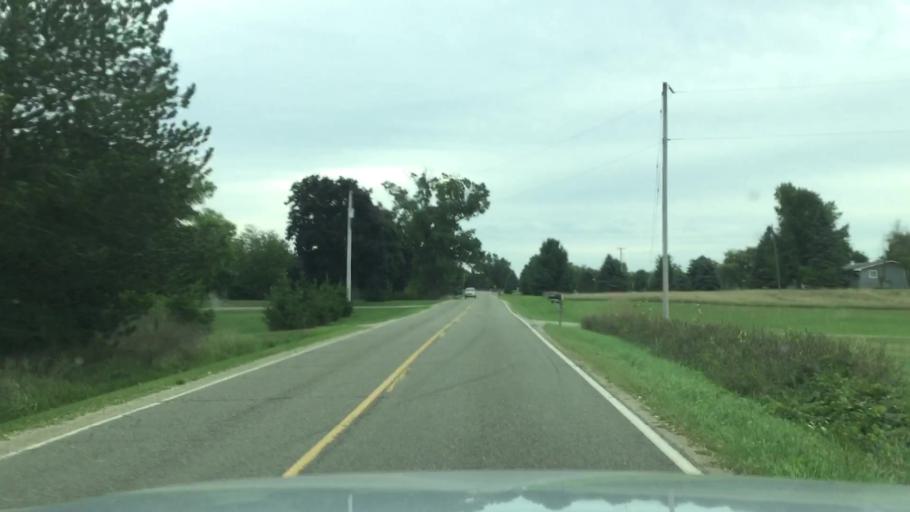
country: US
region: Michigan
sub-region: Shiawassee County
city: Durand
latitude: 42.8350
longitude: -84.0325
